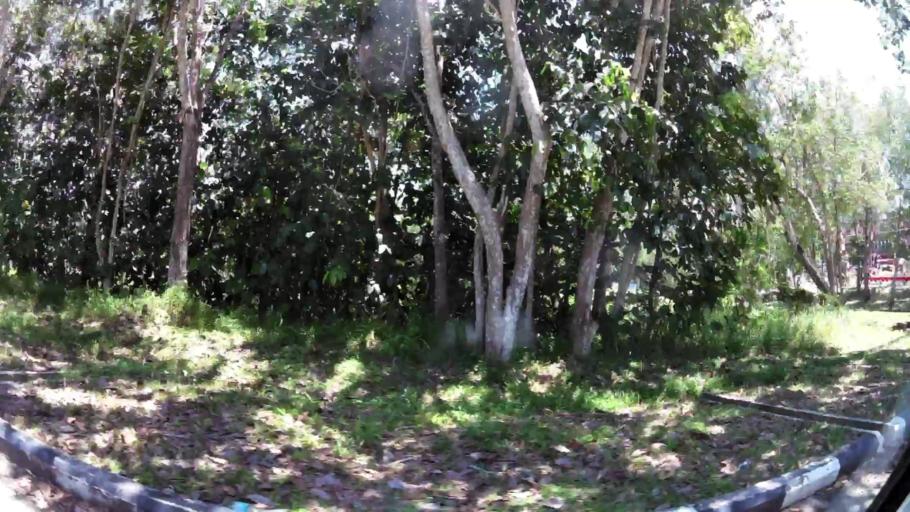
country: BN
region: Brunei and Muara
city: Bandar Seri Begawan
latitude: 4.9214
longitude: 114.9584
